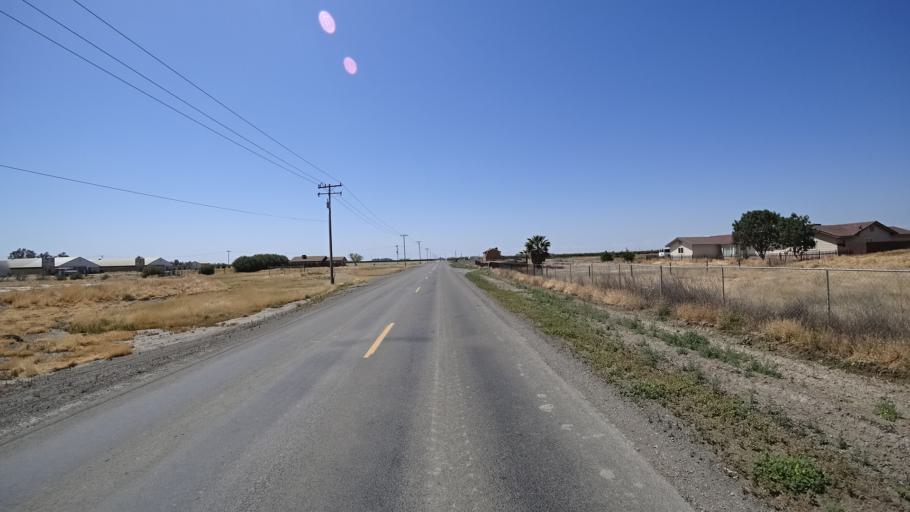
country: US
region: California
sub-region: Kings County
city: Stratford
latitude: 36.2349
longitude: -119.7985
